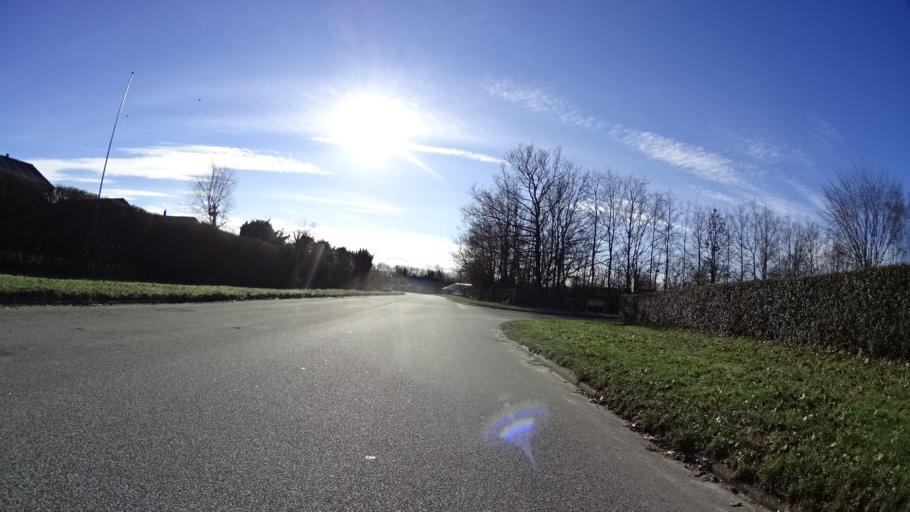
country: DK
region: Central Jutland
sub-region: Arhus Kommune
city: Kolt
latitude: 56.1068
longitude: 10.0767
